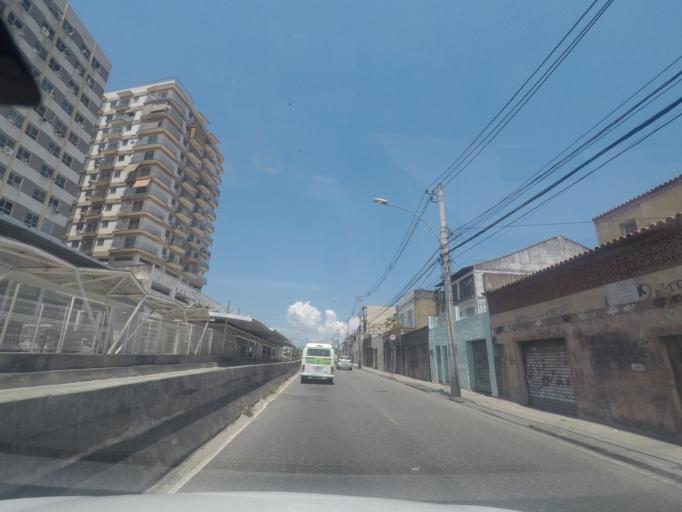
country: BR
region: Rio de Janeiro
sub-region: Duque De Caxias
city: Duque de Caxias
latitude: -22.8421
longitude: -43.2765
